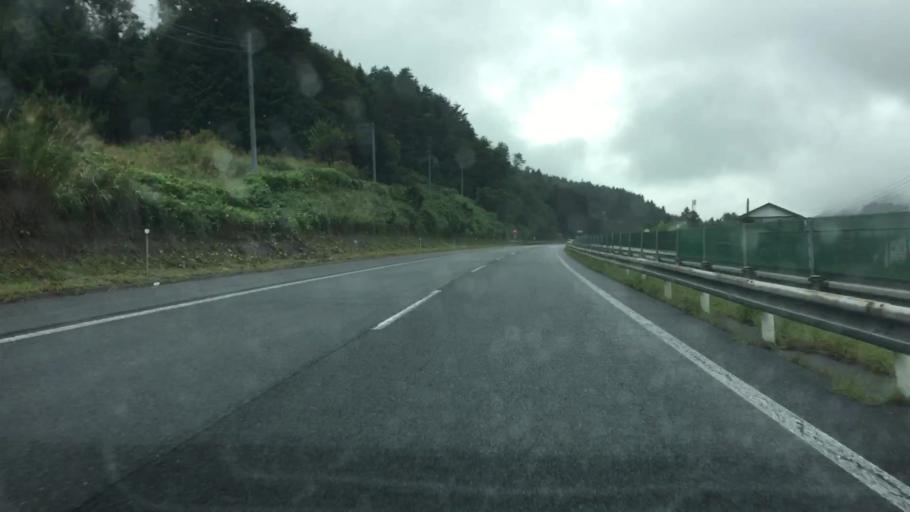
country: JP
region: Yamanashi
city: Otsuki
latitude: 35.5187
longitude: 138.8482
